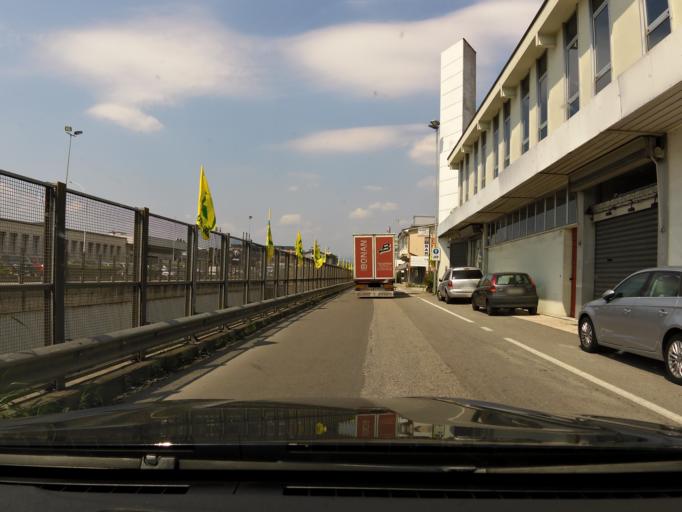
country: IT
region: Veneto
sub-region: Provincia di Verona
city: Beccacivetta-Azzano
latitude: 45.4015
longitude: 10.9734
